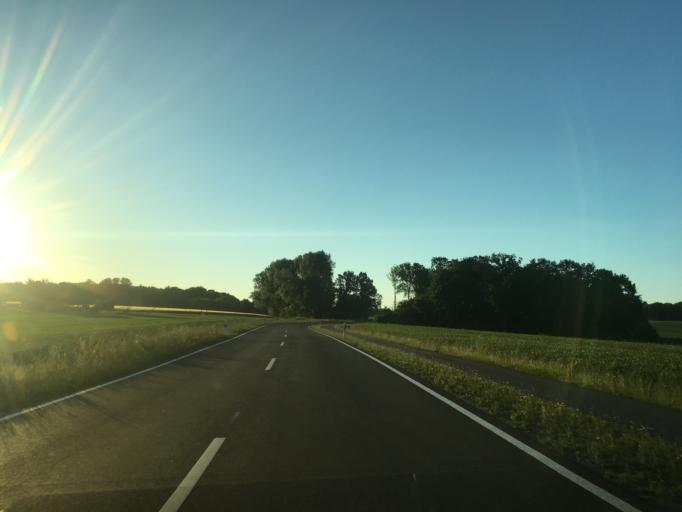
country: DE
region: North Rhine-Westphalia
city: Olfen
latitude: 51.7370
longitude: 7.4016
